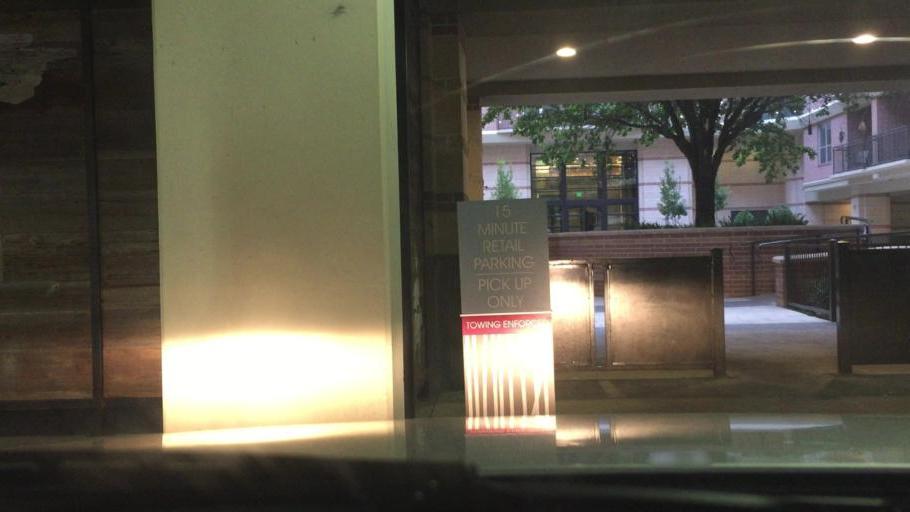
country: US
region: Texas
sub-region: Harris County
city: Hunters Creek Village
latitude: 29.7504
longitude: -95.4788
